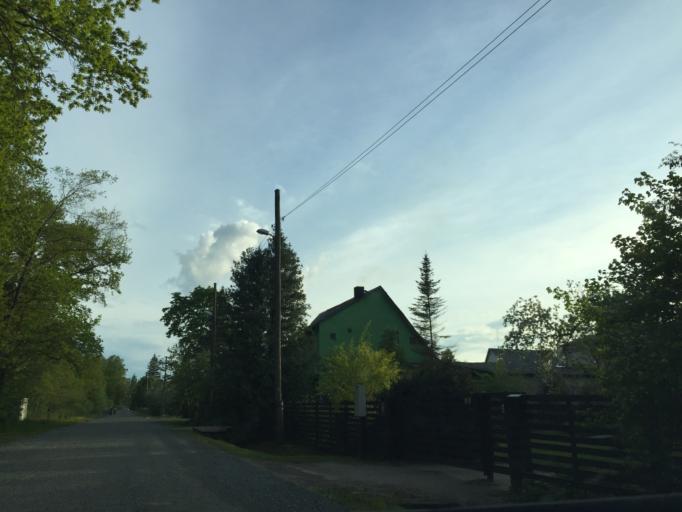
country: LV
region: Ozolnieku
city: Ozolnieki
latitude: 56.6597
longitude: 23.7750
